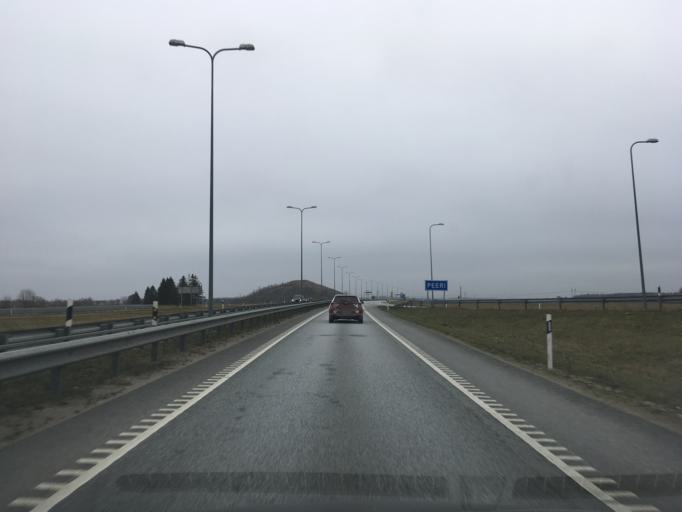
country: EE
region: Ida-Virumaa
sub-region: Kohtla-Jaerve linn
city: Kohtla-Jarve
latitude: 59.4014
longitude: 27.3298
